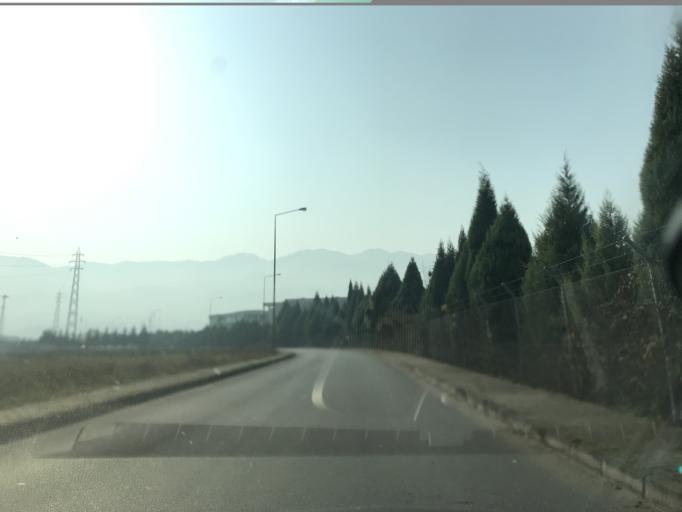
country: TR
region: Duzce
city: Duzce
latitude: 40.7868
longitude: 31.1533
